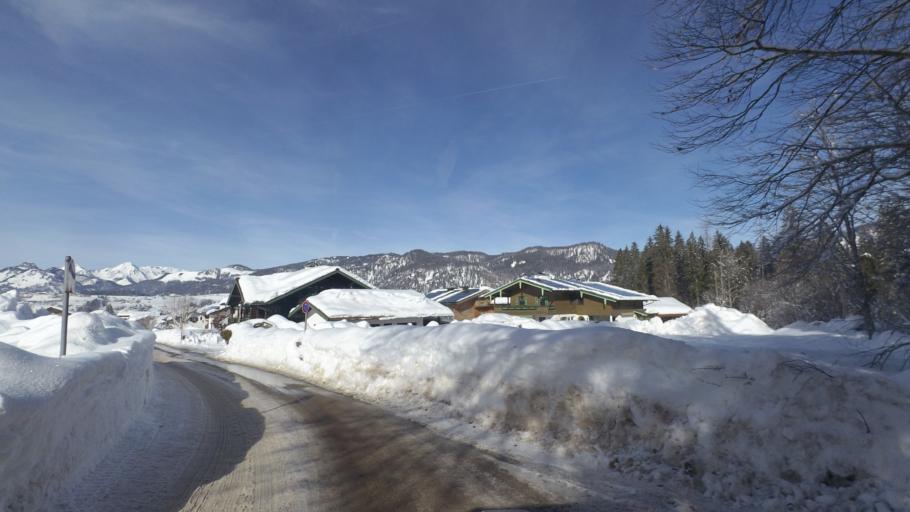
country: DE
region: Bavaria
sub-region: Upper Bavaria
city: Reit im Winkl
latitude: 47.6617
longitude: 12.4787
